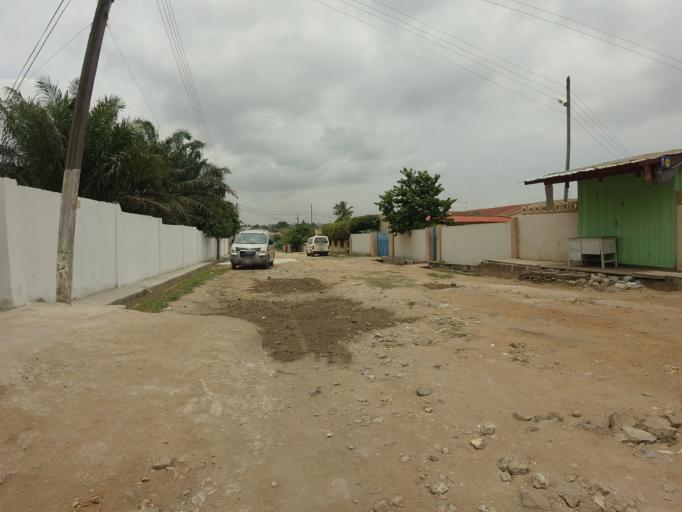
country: GH
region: Greater Accra
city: Dome
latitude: 5.6363
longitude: -0.2326
